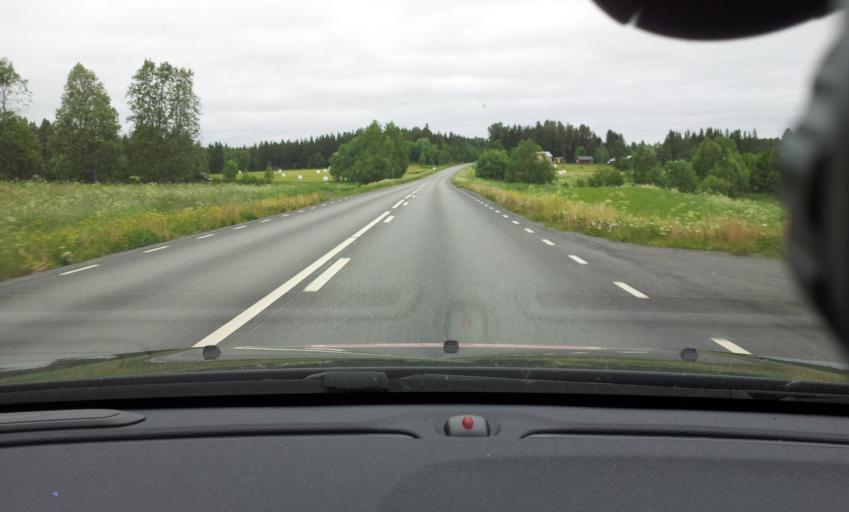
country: SE
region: Jaemtland
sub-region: Krokoms Kommun
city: Krokom
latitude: 63.1016
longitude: 14.2994
